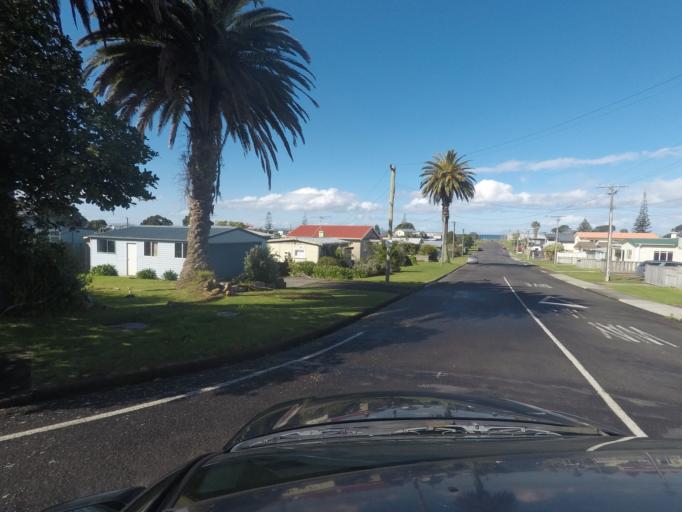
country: NZ
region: Bay of Plenty
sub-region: Western Bay of Plenty District
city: Waihi Beach
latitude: -37.4022
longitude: 175.9365
